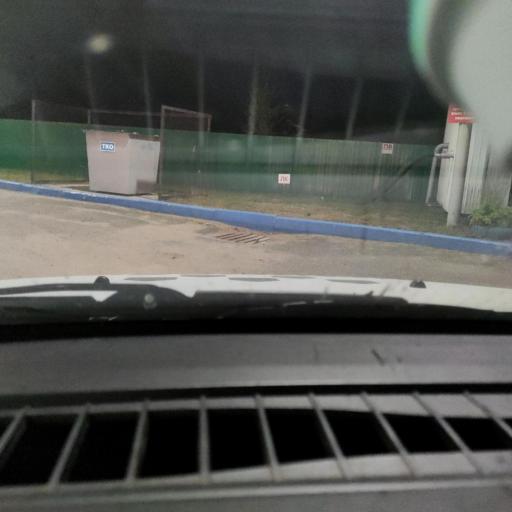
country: RU
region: Kirov
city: Darovskoy
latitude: 58.7638
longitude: 47.9813
